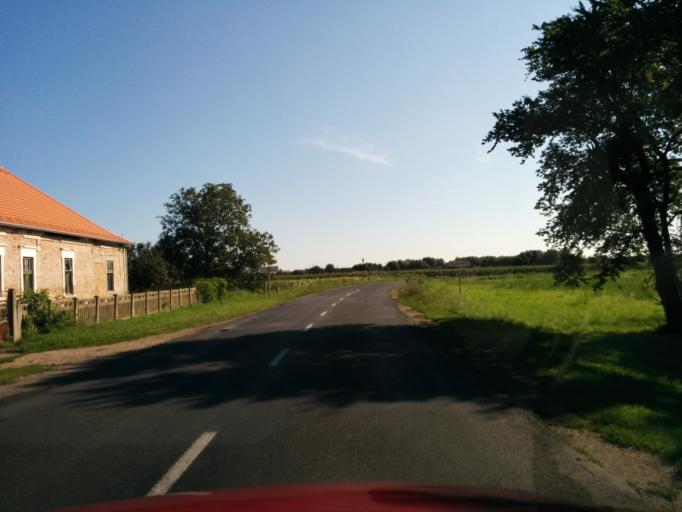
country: HU
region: Vas
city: Buk
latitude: 47.3750
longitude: 16.8659
